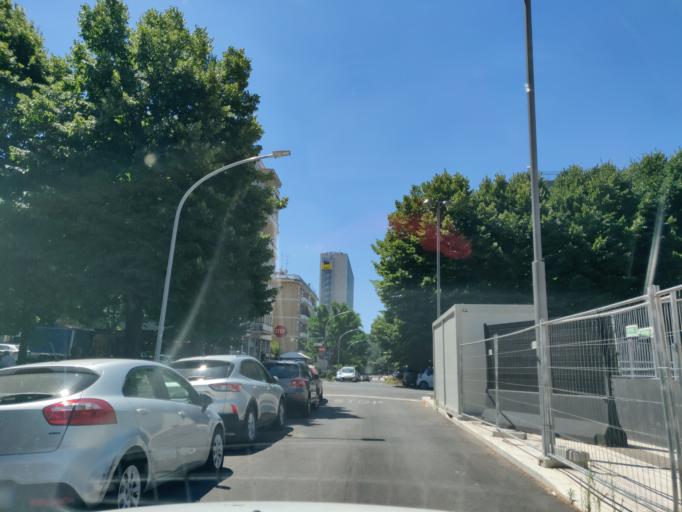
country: IT
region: Latium
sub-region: Citta metropolitana di Roma Capitale
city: Selcetta
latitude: 41.8301
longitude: 12.4728
